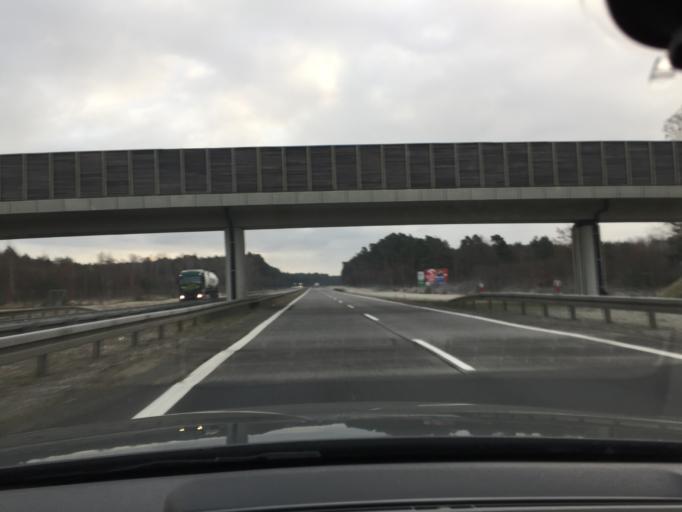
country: PL
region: Lubusz
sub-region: Powiat zarski
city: Trzebiel
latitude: 51.6442
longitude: 14.8470
